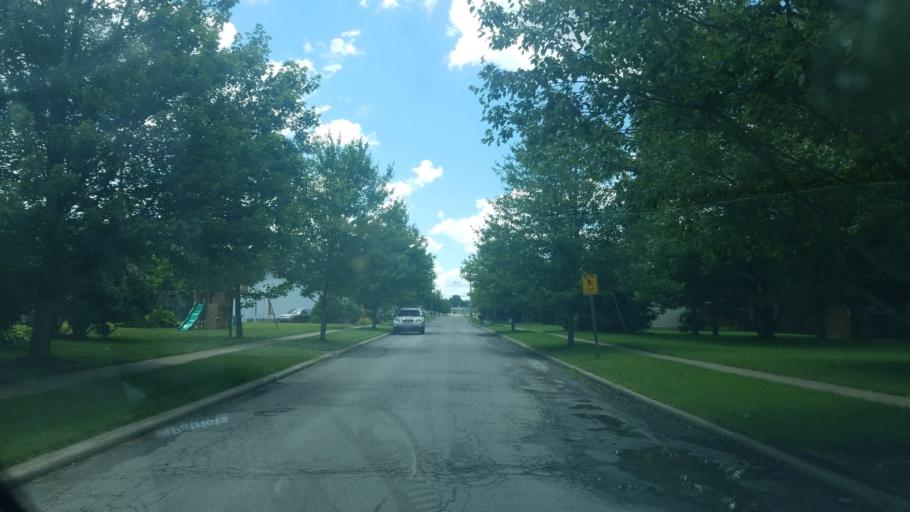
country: US
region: Ohio
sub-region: Huron County
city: New London
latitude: 41.0807
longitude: -82.3897
